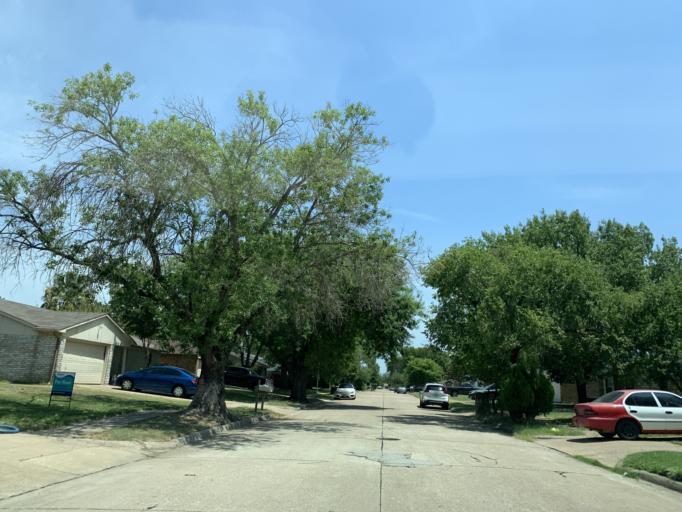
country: US
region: Texas
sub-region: Dallas County
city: Cedar Hill
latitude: 32.6515
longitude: -97.0232
